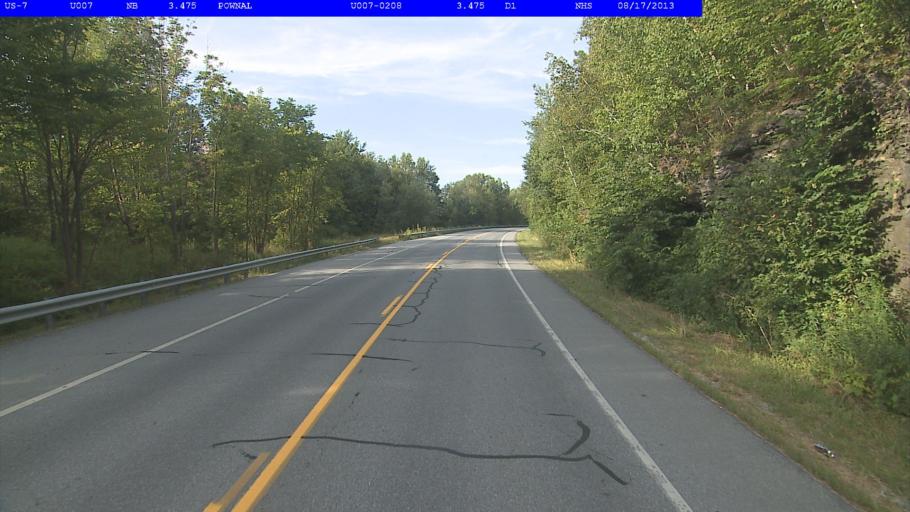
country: US
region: Massachusetts
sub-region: Berkshire County
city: Williamstown
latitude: 42.7849
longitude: -73.2420
